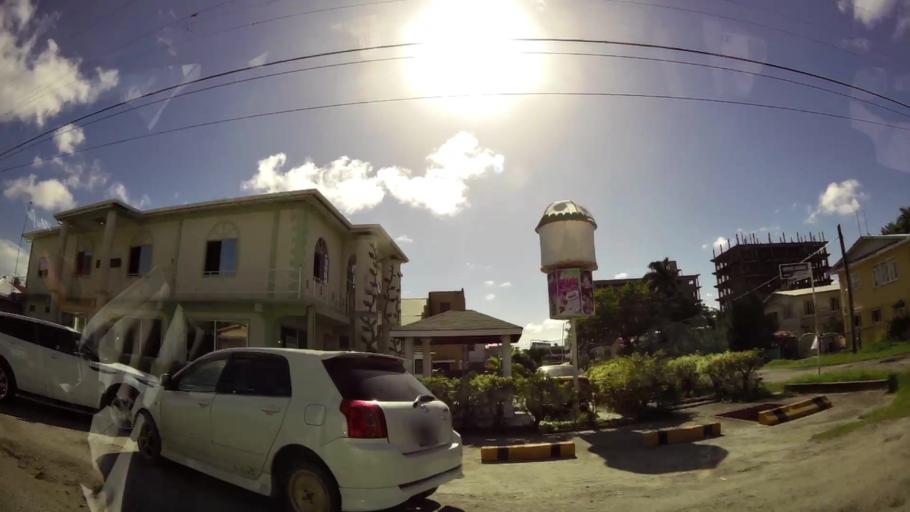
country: GY
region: Demerara-Mahaica
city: Georgetown
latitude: 6.8160
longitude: -58.1339
